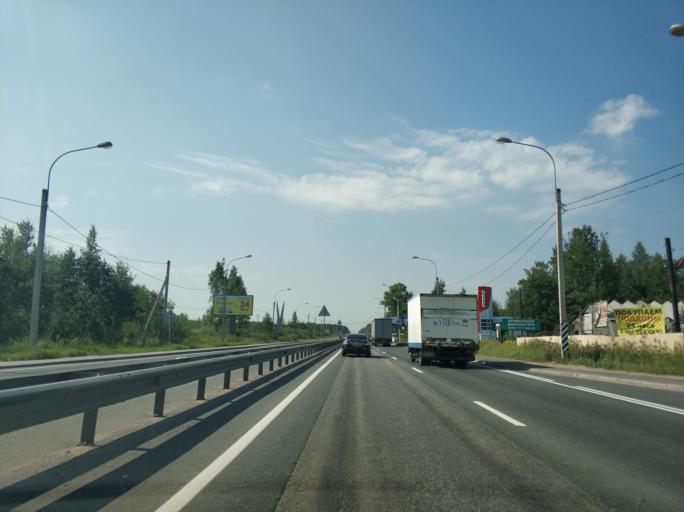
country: RU
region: Leningrad
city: Yanino Vtoroye
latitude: 60.0104
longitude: 30.5771
